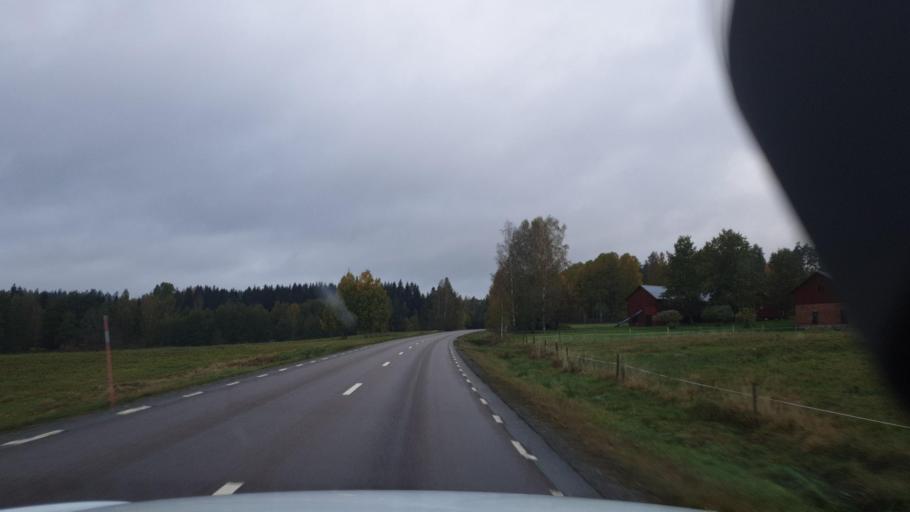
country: SE
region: Vaermland
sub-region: Arvika Kommun
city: Arvika
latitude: 59.6369
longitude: 12.7932
